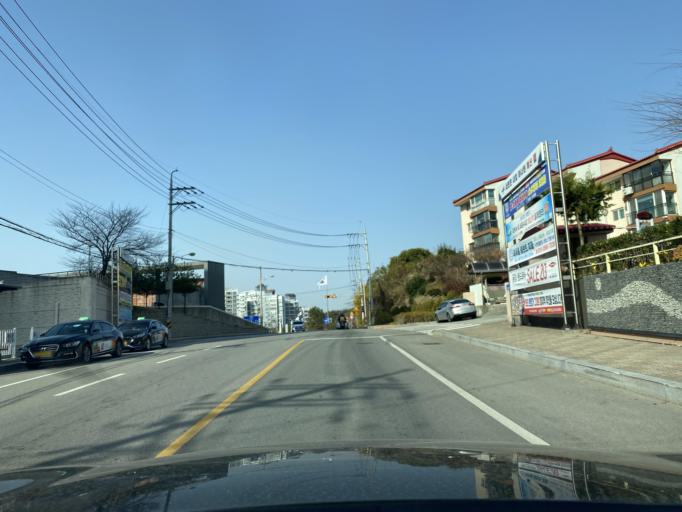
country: KR
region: Chungcheongnam-do
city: Yesan
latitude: 36.6861
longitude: 126.8448
